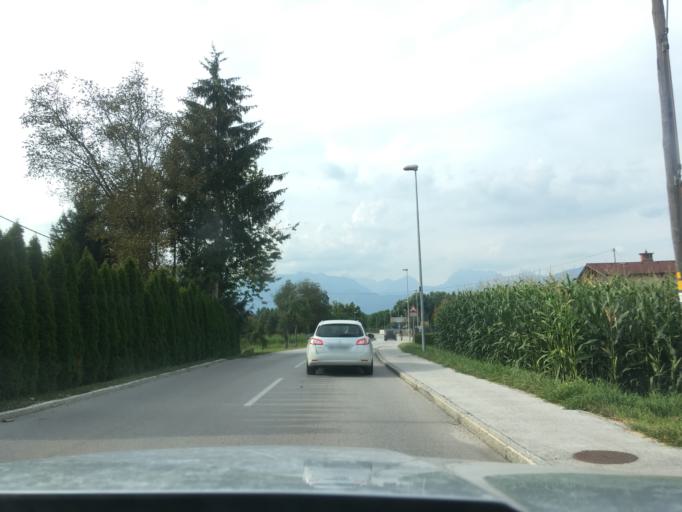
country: SI
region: Domzale
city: Radomlje
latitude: 46.1798
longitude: 14.6091
